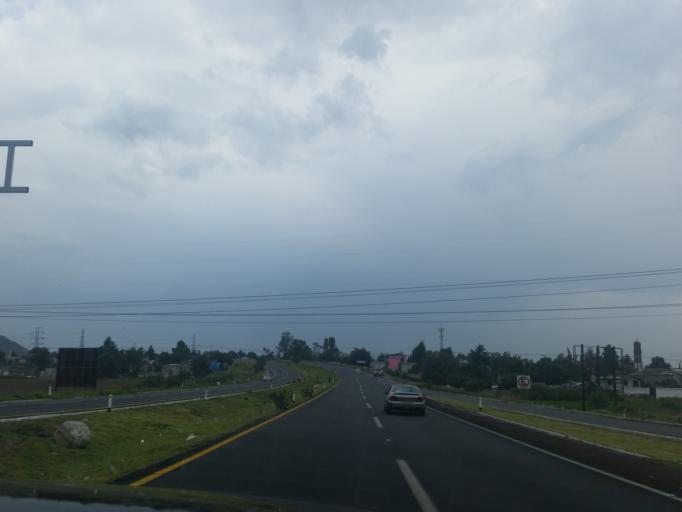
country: MX
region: Morelos
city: Teotihuacan de Arista
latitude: 19.6711
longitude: -98.8670
